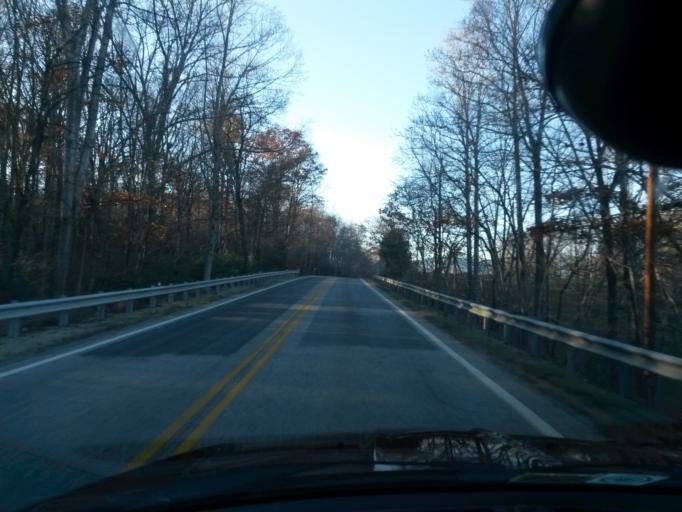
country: US
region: Virginia
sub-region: Amherst County
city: Amherst
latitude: 37.6436
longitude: -79.1232
